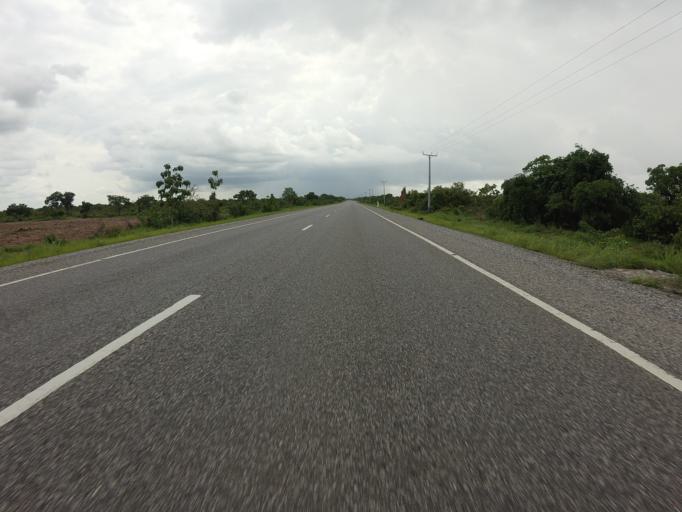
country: GH
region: Northern
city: Tamale
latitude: 9.1322
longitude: -1.3162
